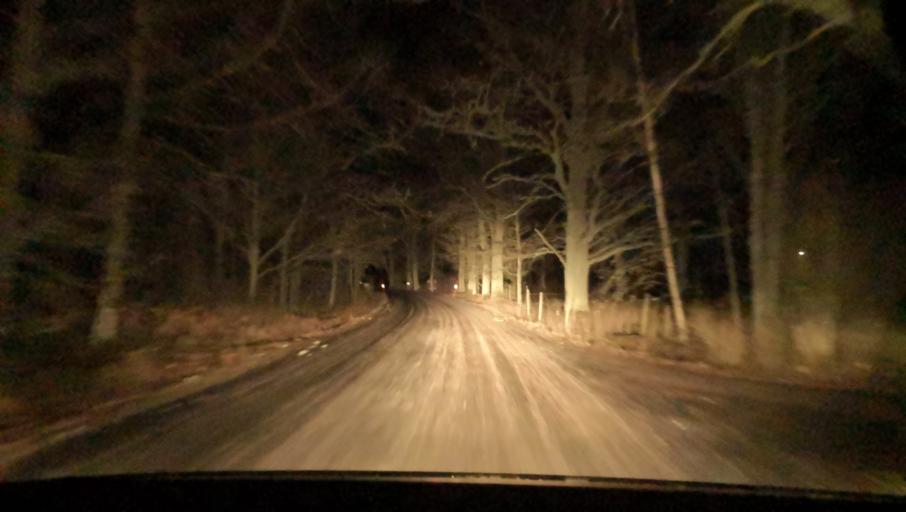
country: SE
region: Vaestmanland
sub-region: Vasteras
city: Tillberga
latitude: 59.6691
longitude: 16.6404
